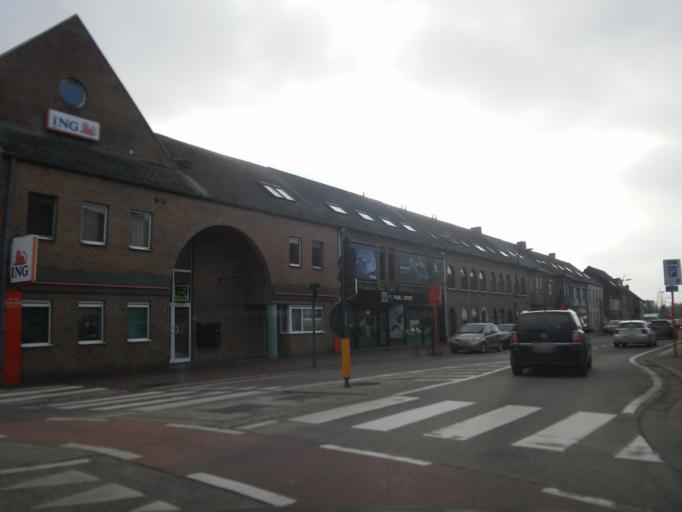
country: BE
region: Flanders
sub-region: Provincie Antwerpen
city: Herselt
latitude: 51.0552
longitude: 4.8849
